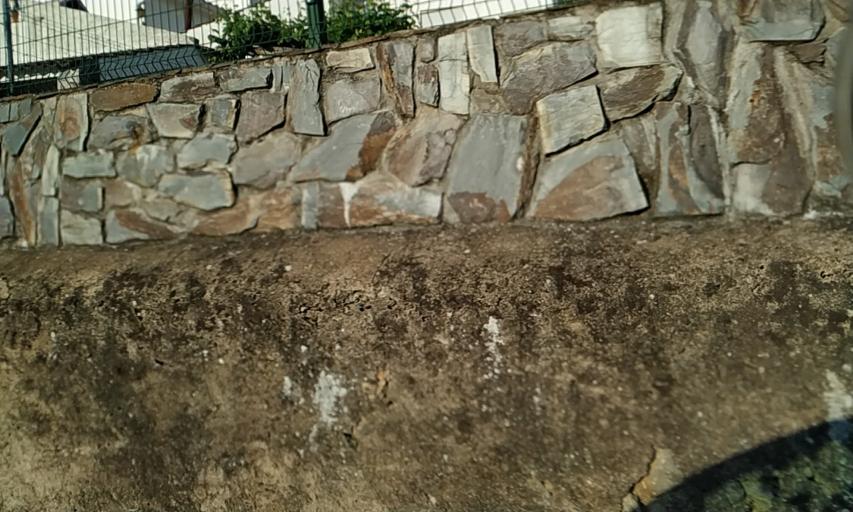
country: PT
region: Portalegre
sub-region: Portalegre
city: Portalegre
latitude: 39.3121
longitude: -7.4414
